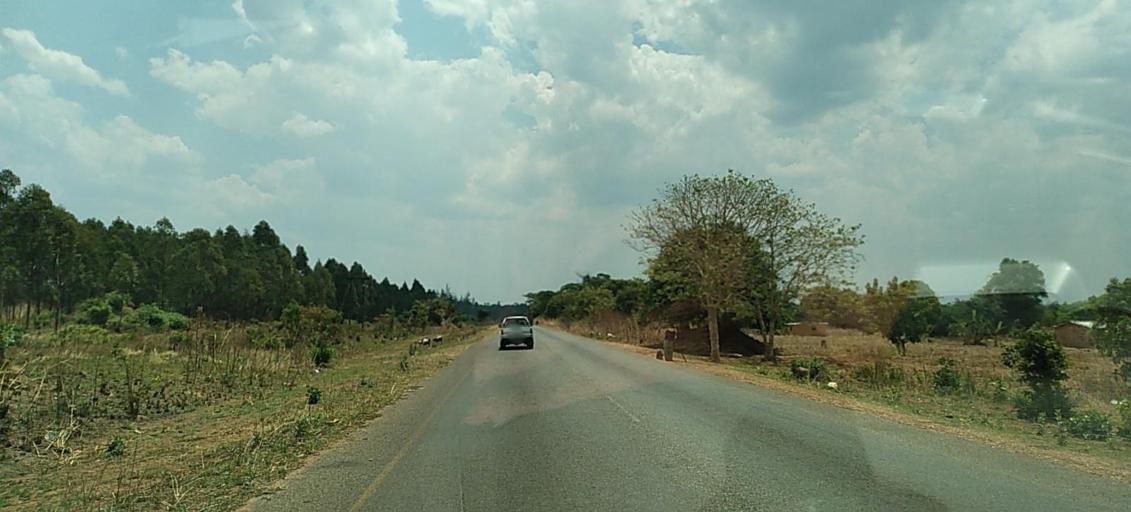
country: ZM
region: Copperbelt
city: Kalulushi
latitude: -12.8375
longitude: 27.9334
